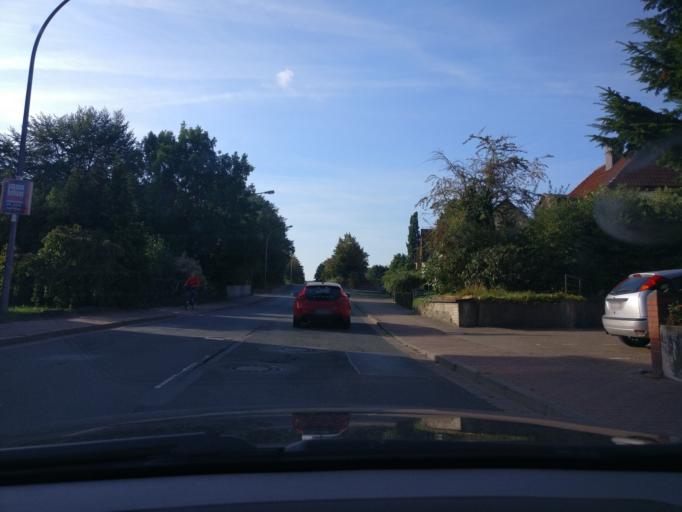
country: DE
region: Lower Saxony
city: Melle
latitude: 52.1947
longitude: 8.3357
